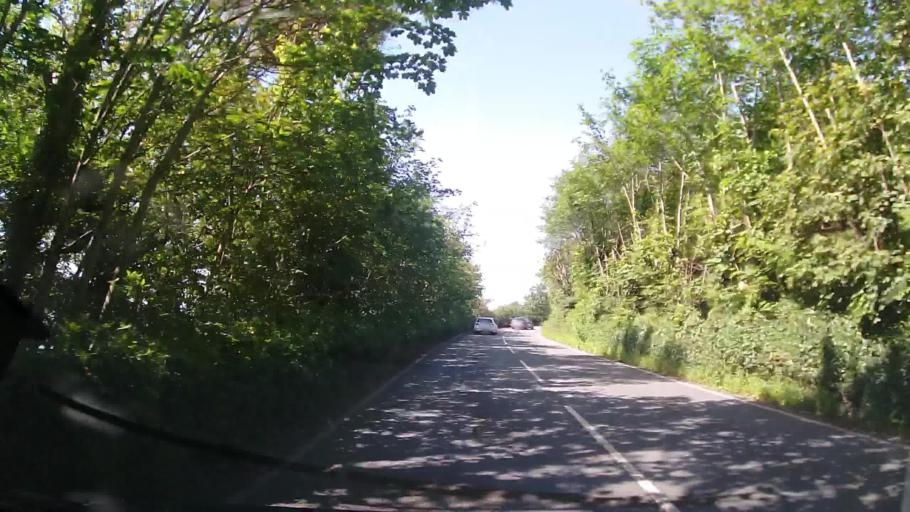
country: GB
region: Wales
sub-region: Gwynedd
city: Tywyn
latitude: 52.5477
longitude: -4.0205
